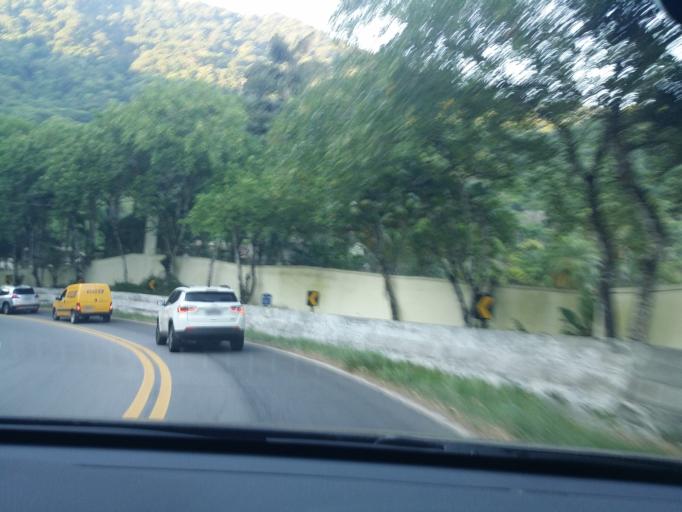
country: BR
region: Sao Paulo
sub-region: Sao Sebastiao
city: Sao Sebastiao
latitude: -23.7878
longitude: -45.5888
